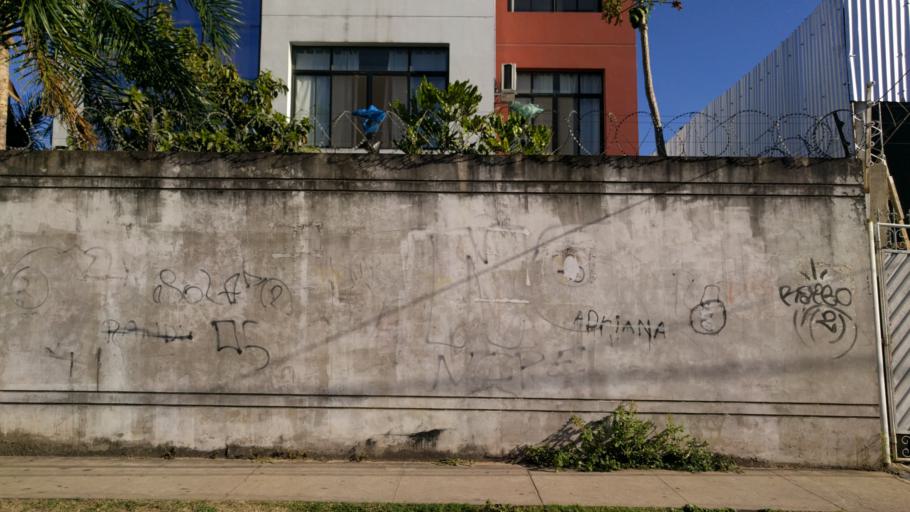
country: BO
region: Santa Cruz
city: Santa Cruz de la Sierra
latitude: -17.7715
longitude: -63.2088
